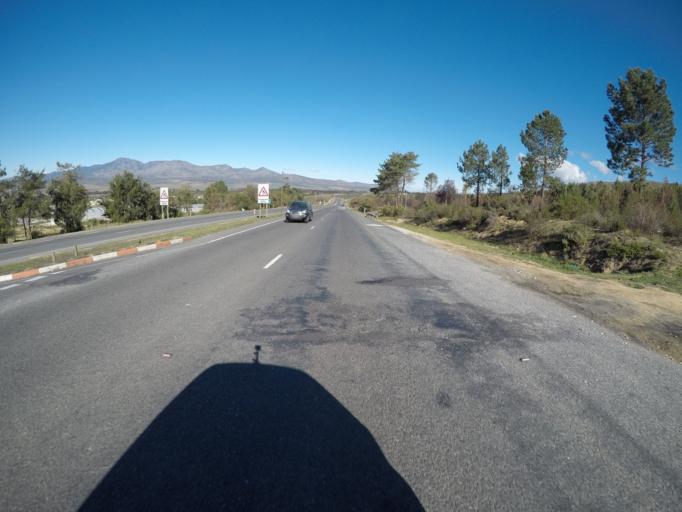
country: ZA
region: Western Cape
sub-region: Overberg District Municipality
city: Grabouw
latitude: -34.2227
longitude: 19.1877
